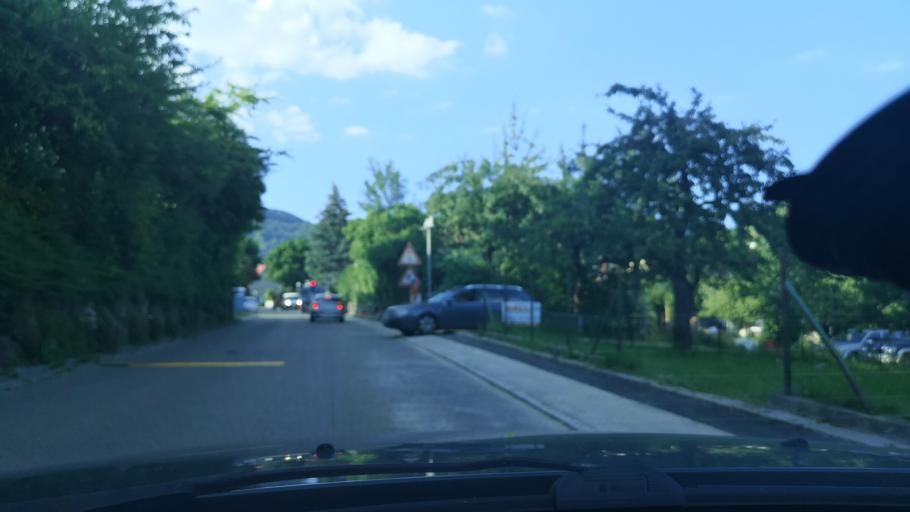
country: DE
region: Baden-Wuerttemberg
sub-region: Regierungsbezirk Stuttgart
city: Deggingen
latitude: 48.6128
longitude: 9.7359
